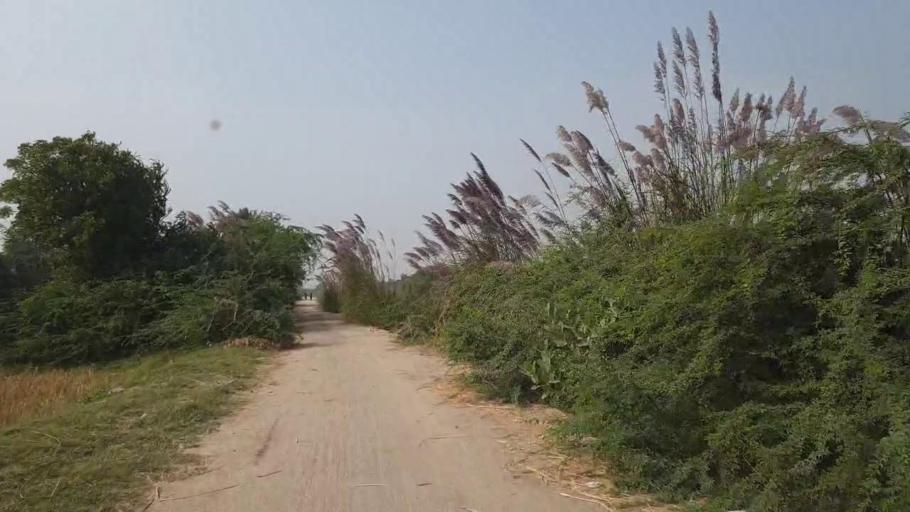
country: PK
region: Sindh
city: Matli
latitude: 25.0319
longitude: 68.5945
